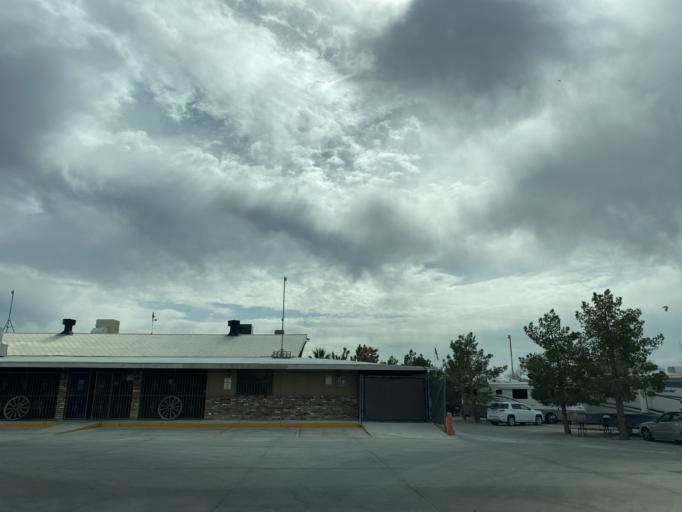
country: US
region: Nevada
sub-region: Clark County
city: Sunrise Manor
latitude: 36.2226
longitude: -115.0837
